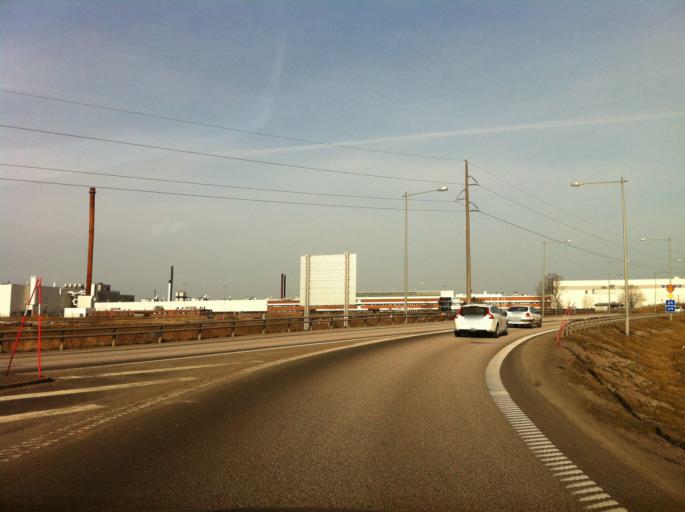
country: SE
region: Vaestra Goetaland
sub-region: Skovde Kommun
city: Skoevde
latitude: 58.3750
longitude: 13.8579
